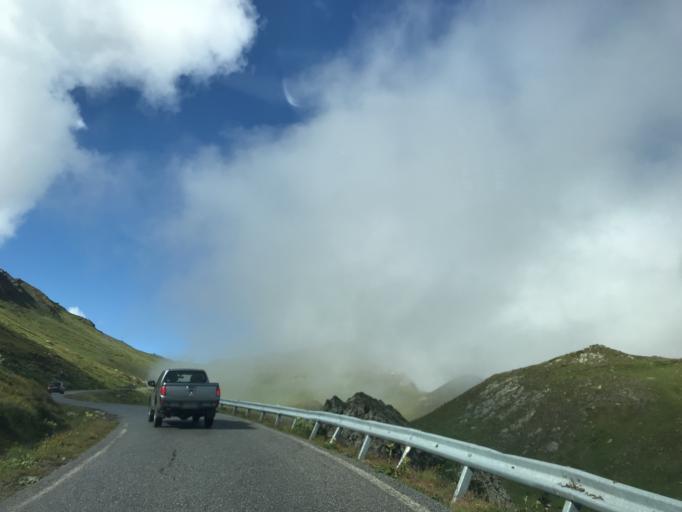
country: IT
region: Piedmont
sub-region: Provincia di Cuneo
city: Pontechianale
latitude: 44.6785
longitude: 6.9782
